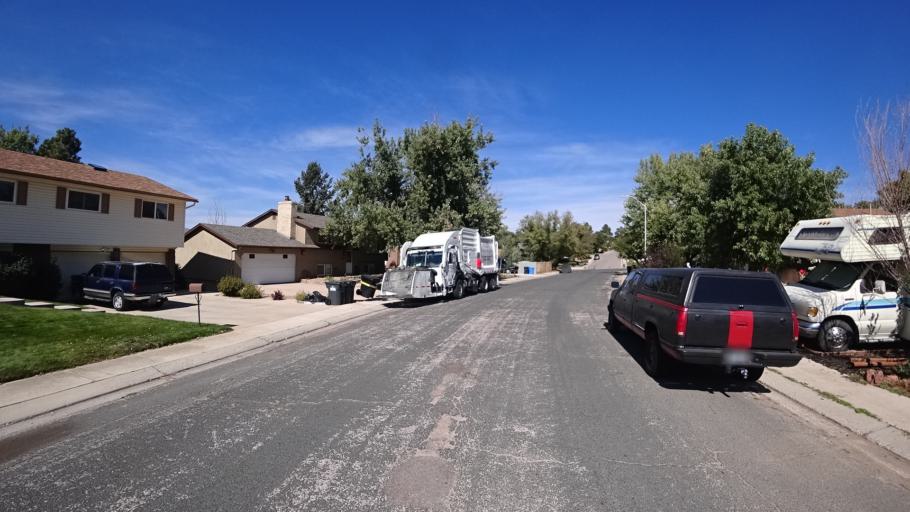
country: US
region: Colorado
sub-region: El Paso County
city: Cimarron Hills
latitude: 38.9140
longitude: -104.7674
